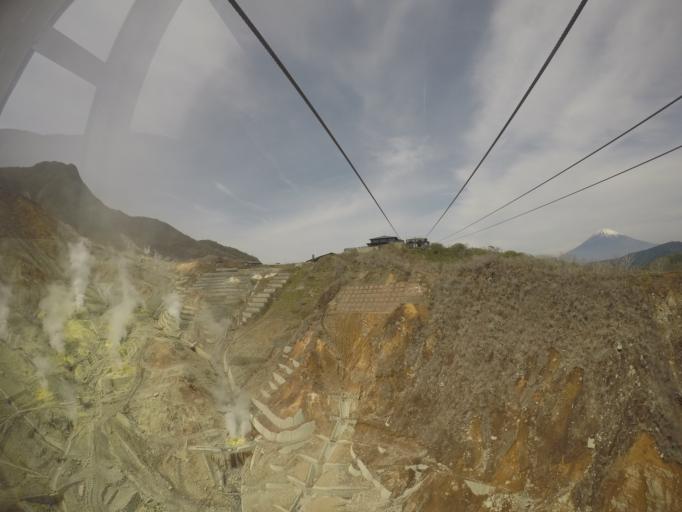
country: JP
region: Kanagawa
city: Hakone
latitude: 35.2450
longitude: 139.0228
